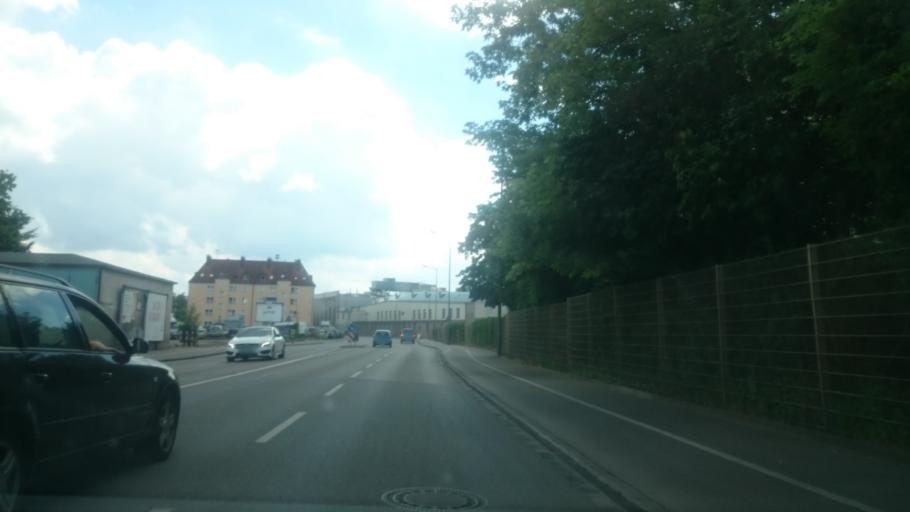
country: DE
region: Bavaria
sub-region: Swabia
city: Augsburg
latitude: 48.3845
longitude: 10.8882
